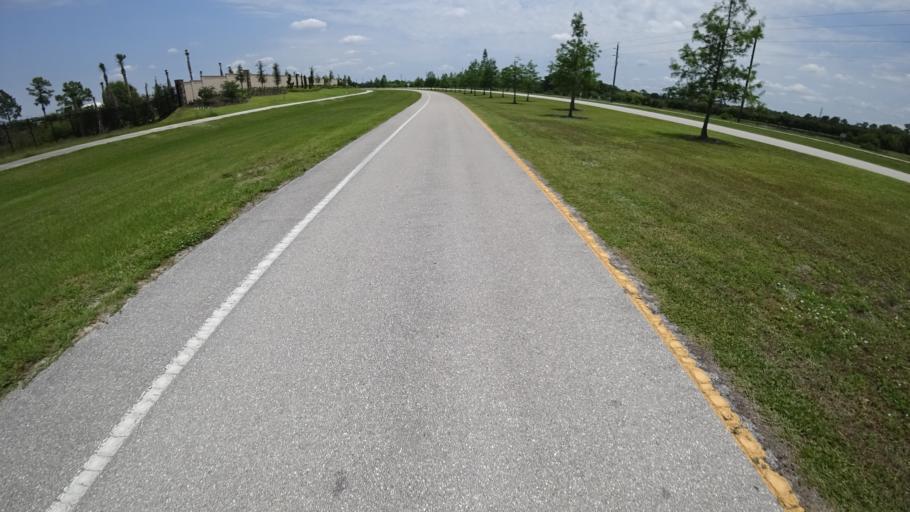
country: US
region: Florida
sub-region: Sarasota County
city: The Meadows
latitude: 27.3862
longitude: -82.3733
